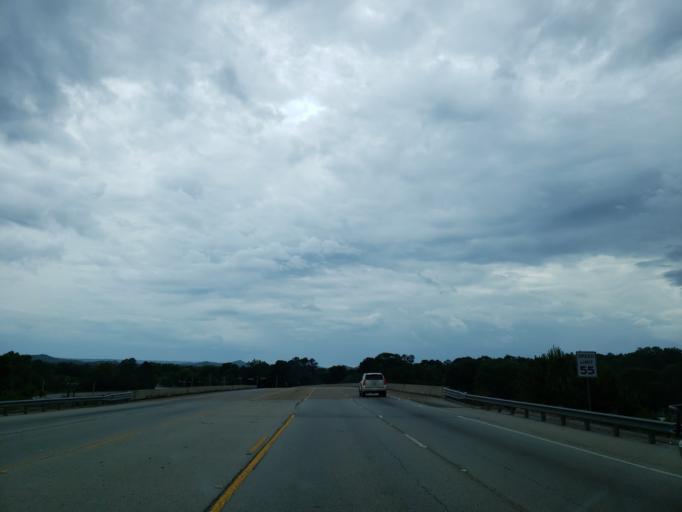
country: US
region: Georgia
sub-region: Polk County
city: Cedartown
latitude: 33.9904
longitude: -85.2502
